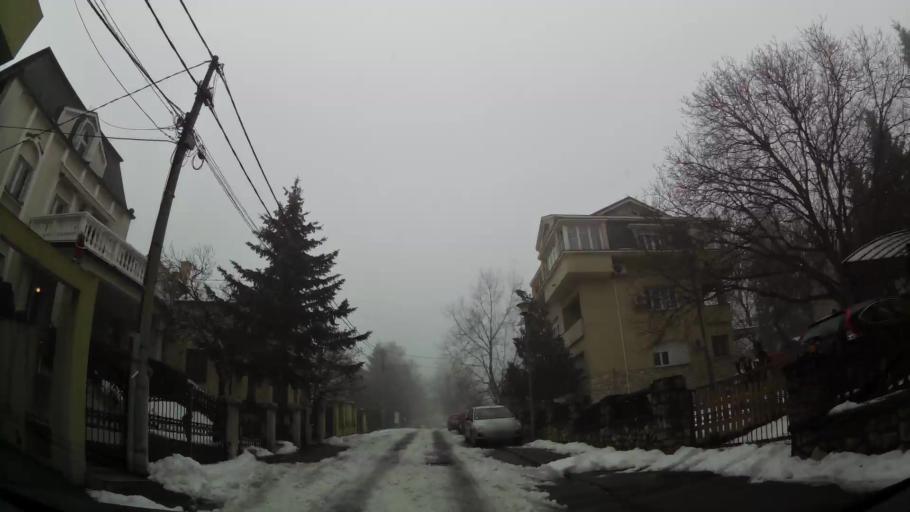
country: RS
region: Central Serbia
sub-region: Belgrade
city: Savski Venac
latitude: 44.7718
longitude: 20.4570
